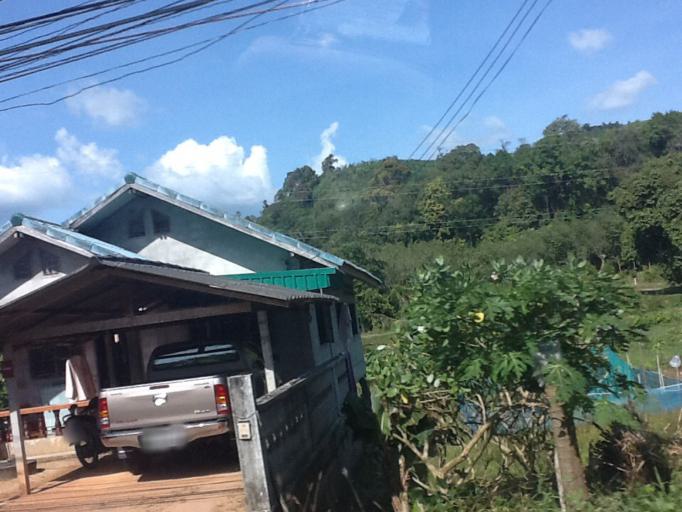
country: TH
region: Phuket
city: Thalang
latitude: 8.1235
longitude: 98.3229
